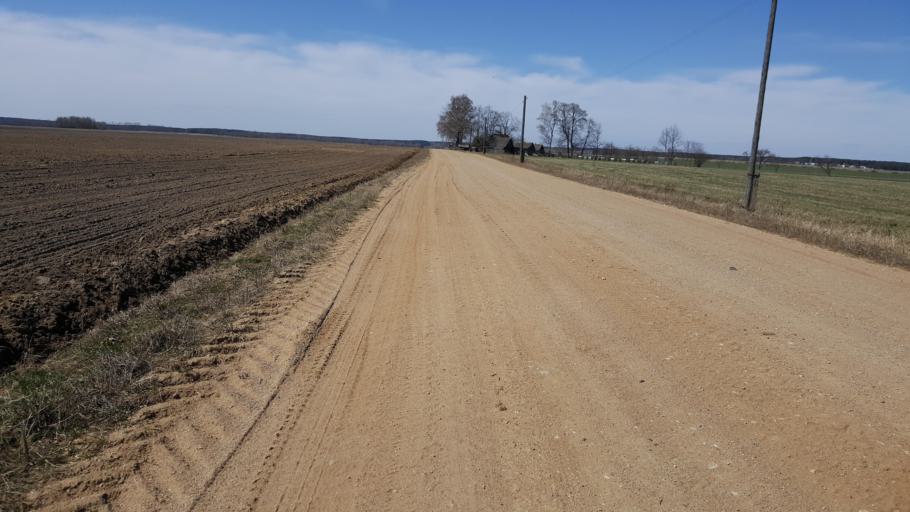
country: BY
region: Brest
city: Zhabinka
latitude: 52.2958
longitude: 23.9152
